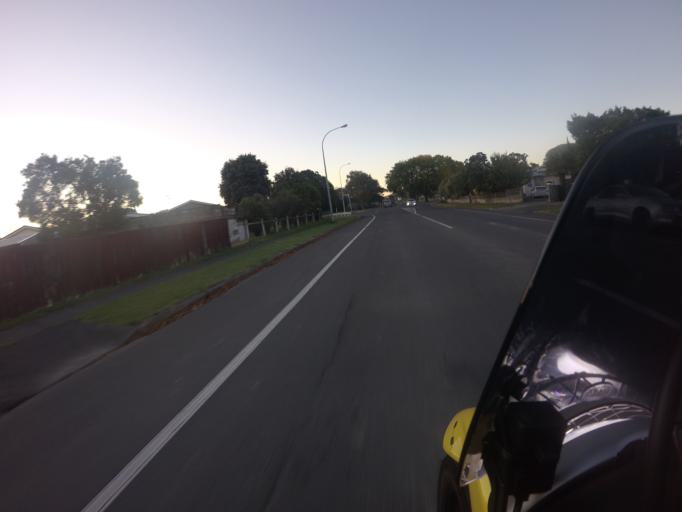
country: NZ
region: Gisborne
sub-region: Gisborne District
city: Gisborne
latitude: -38.6757
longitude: 178.0479
